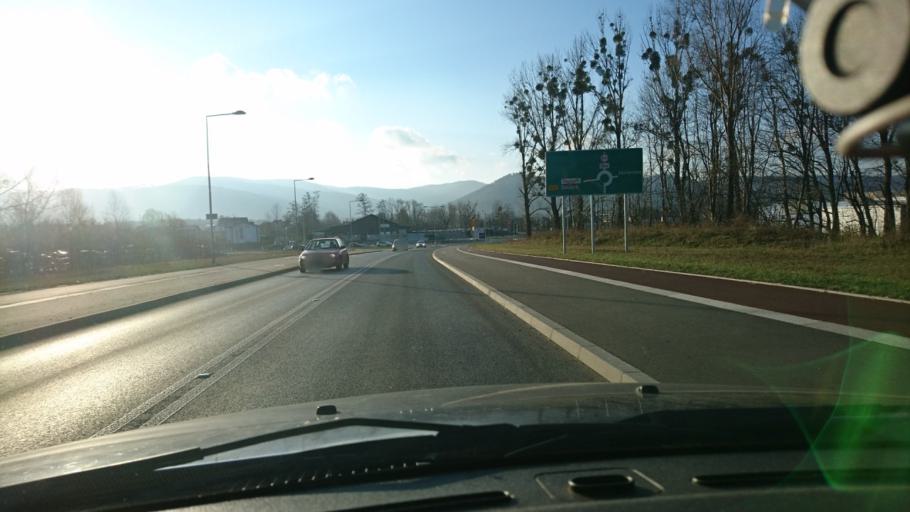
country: PL
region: Silesian Voivodeship
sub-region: Powiat bielski
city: Jaworze
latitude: 49.8088
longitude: 18.9751
